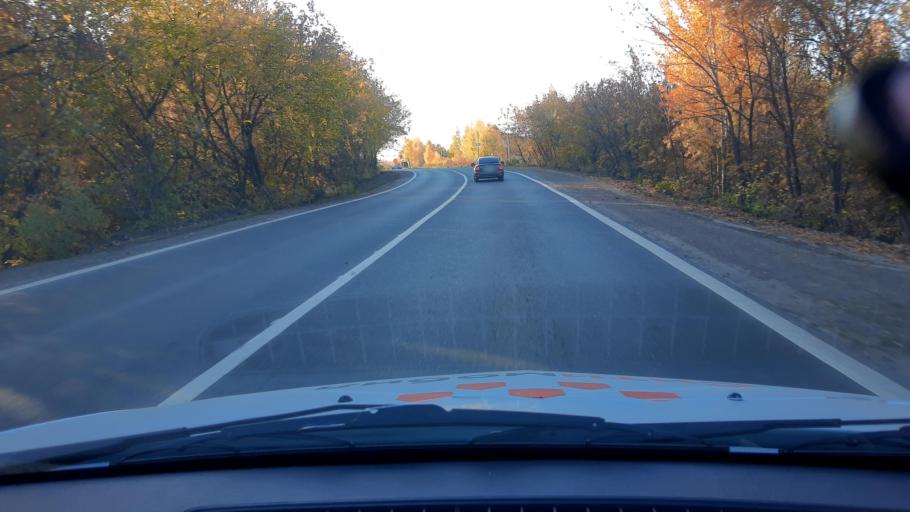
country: RU
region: Bashkortostan
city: Iglino
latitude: 54.7757
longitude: 56.2394
